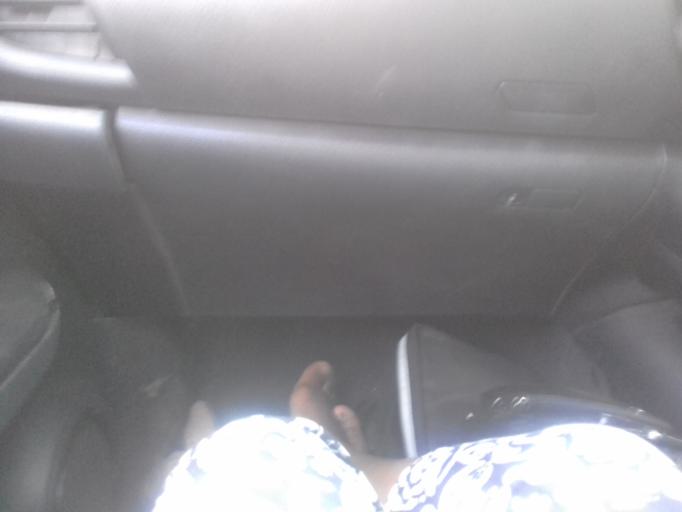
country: LS
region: Thaba-Tseka
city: Thaba-Tseka
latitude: -29.5148
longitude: 28.3253
